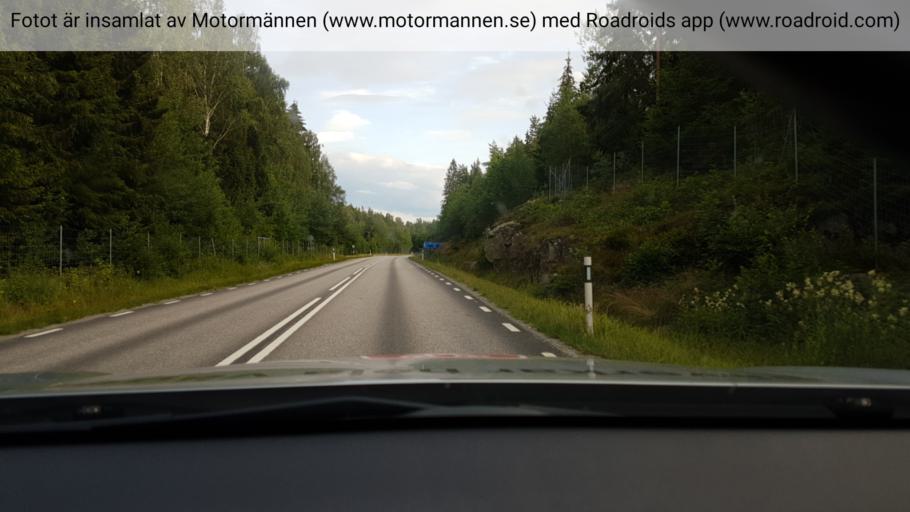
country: SE
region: Vaestra Goetaland
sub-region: Fargelanda Kommun
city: Faergelanda
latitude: 58.4628
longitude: 12.0228
